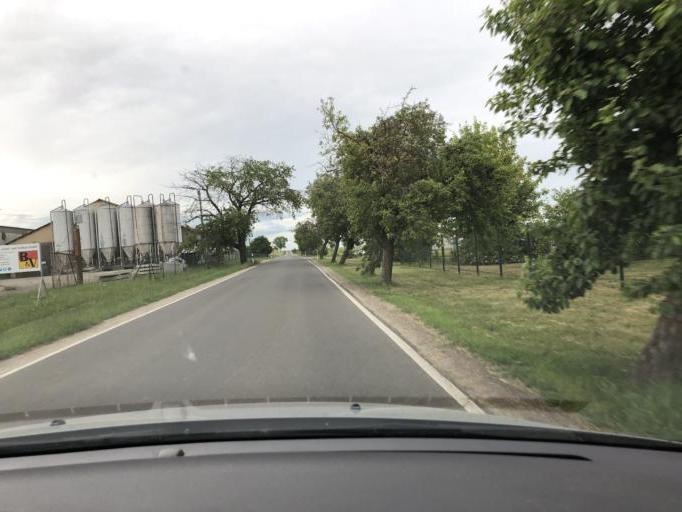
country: DE
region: Thuringia
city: Pfiffelbach
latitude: 51.0672
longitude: 11.4441
